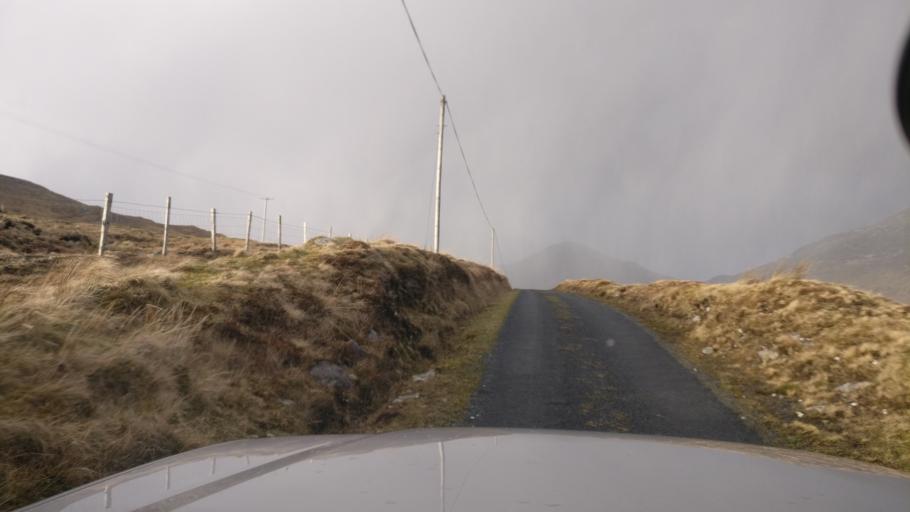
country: IE
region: Connaught
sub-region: County Galway
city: Clifden
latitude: 53.4807
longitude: -9.6958
